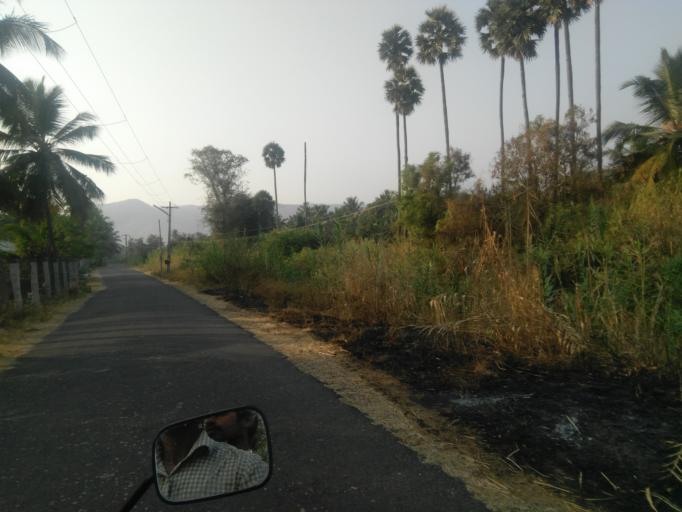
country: IN
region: Tamil Nadu
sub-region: Coimbatore
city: Karamadai
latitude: 11.2158
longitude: 76.8881
